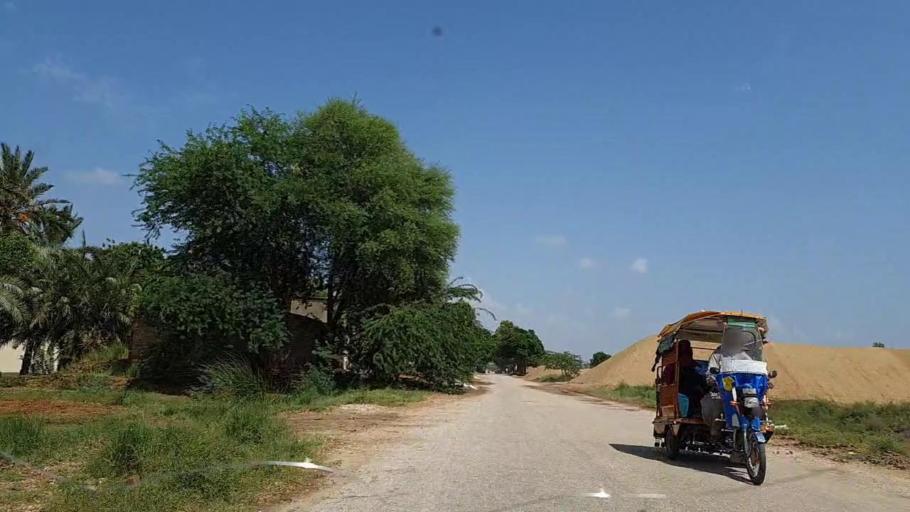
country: PK
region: Sindh
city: Pad Idan
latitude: 26.7985
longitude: 68.2319
